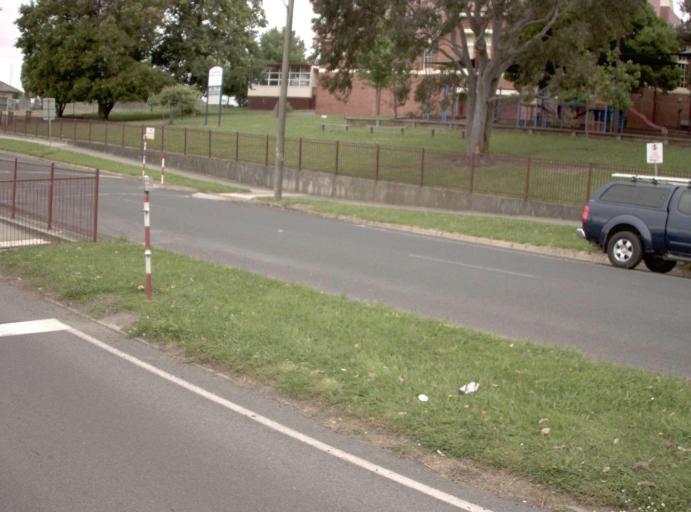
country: AU
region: Victoria
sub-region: Bass Coast
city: North Wonthaggi
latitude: -38.4345
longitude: 145.8254
